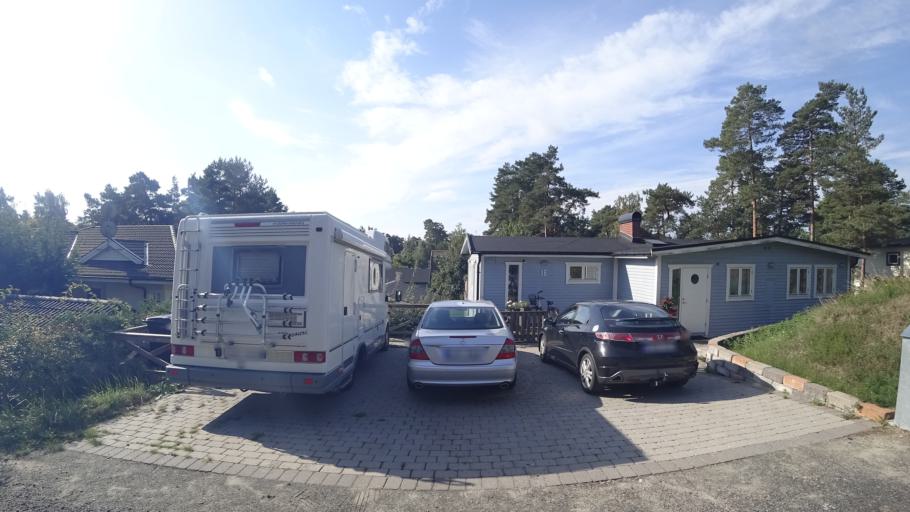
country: SE
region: Skane
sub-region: Kristianstads Kommun
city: Ahus
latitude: 55.9194
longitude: 14.3022
